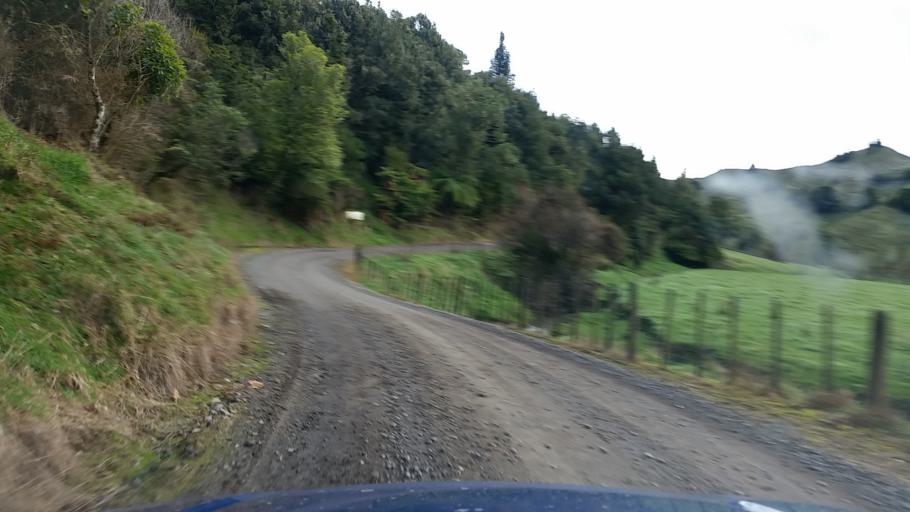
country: NZ
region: Taranaki
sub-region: New Plymouth District
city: Waitara
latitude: -39.0942
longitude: 174.8397
